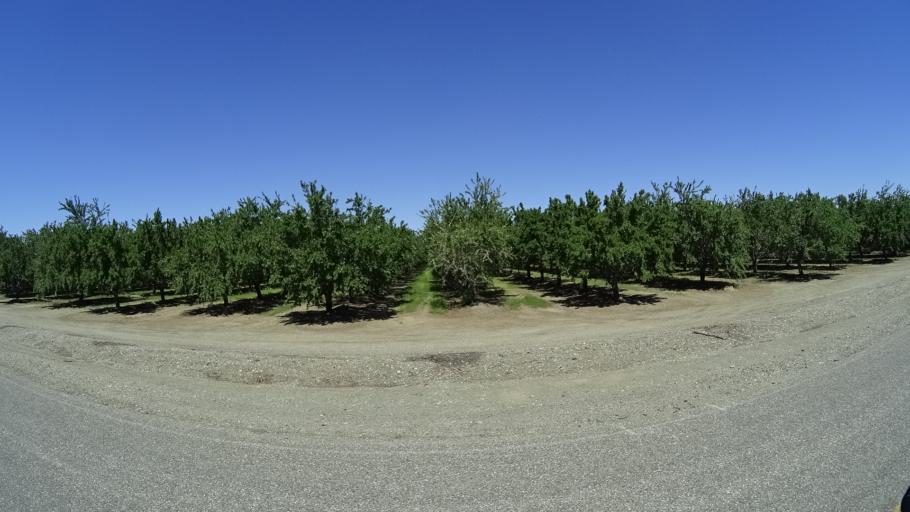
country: US
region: California
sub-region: Glenn County
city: Orland
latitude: 39.7250
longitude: -122.1173
